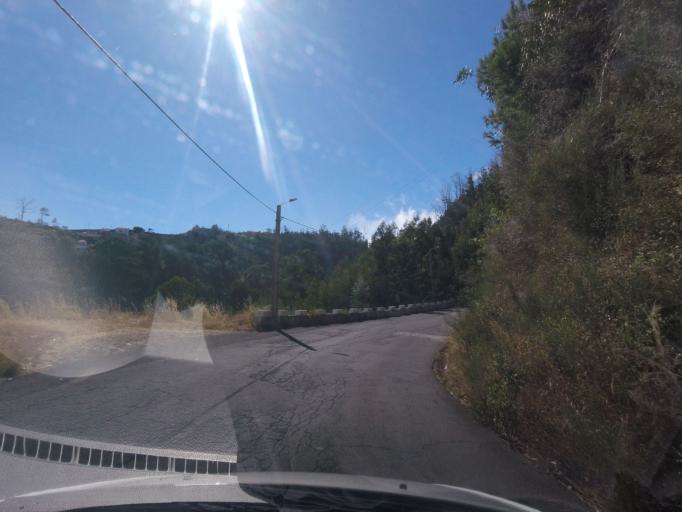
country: PT
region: Madeira
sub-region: Santa Cruz
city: Camacha
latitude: 32.6897
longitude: -16.8470
